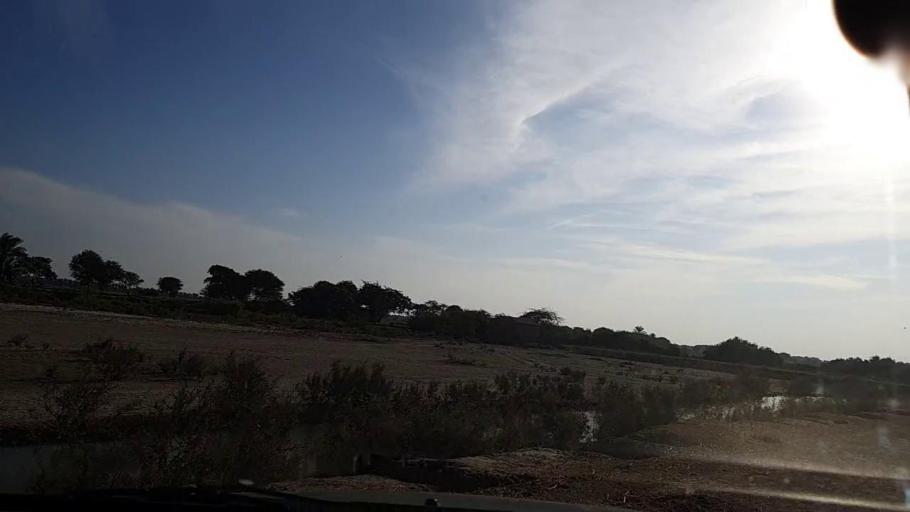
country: PK
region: Sindh
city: Mirpur Batoro
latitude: 24.6535
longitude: 68.3094
